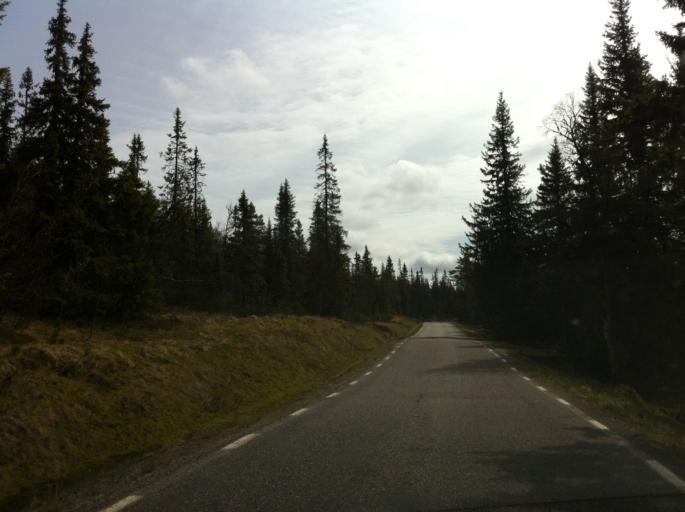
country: NO
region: Hedmark
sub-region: Engerdal
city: Engerdal
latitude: 62.3025
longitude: 12.8009
